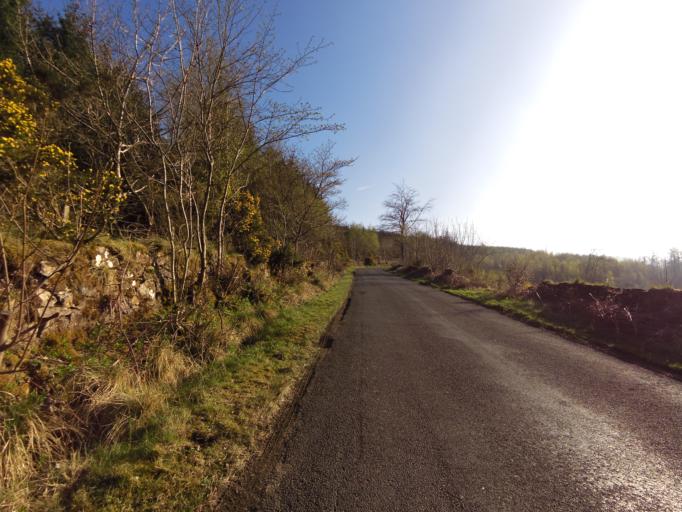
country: GB
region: Scotland
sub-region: Fife
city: Falkland
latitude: 56.2488
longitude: -3.2335
